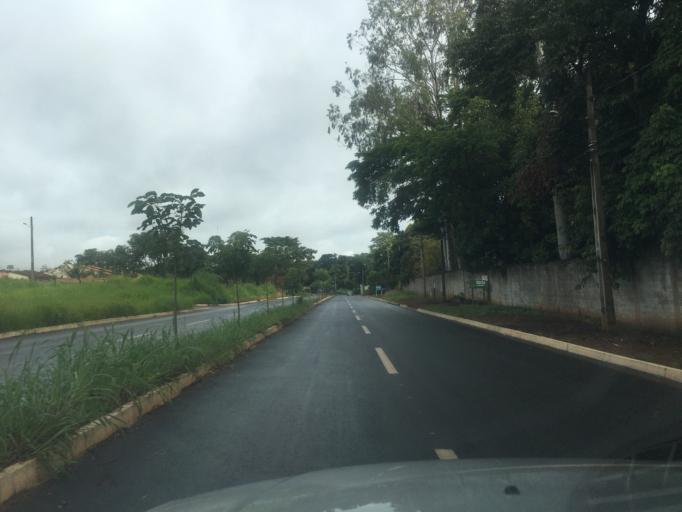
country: BR
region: Goias
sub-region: Aparecida De Goiania
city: Aparecida de Goiania
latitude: -16.8009
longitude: -49.2488
